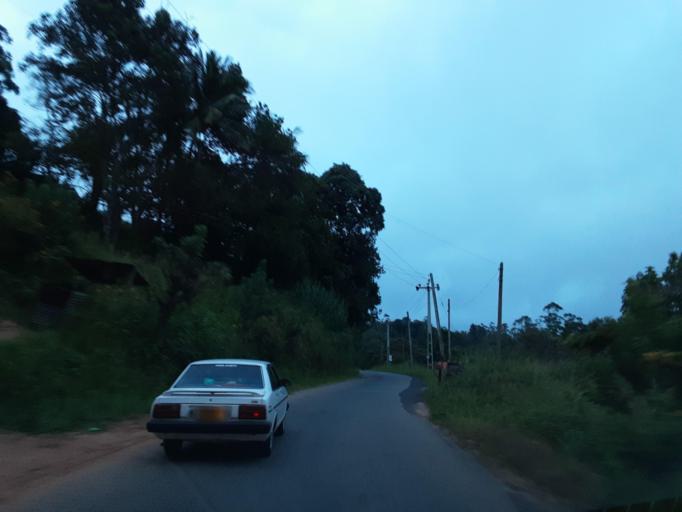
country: LK
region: Uva
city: Haputale
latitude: 6.9080
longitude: 80.9231
